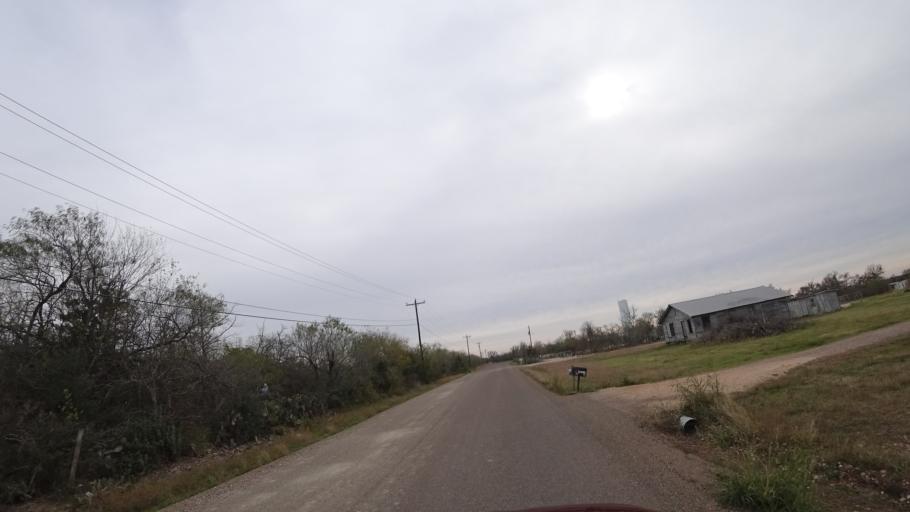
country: US
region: Texas
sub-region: Travis County
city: Garfield
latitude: 30.1138
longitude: -97.5710
